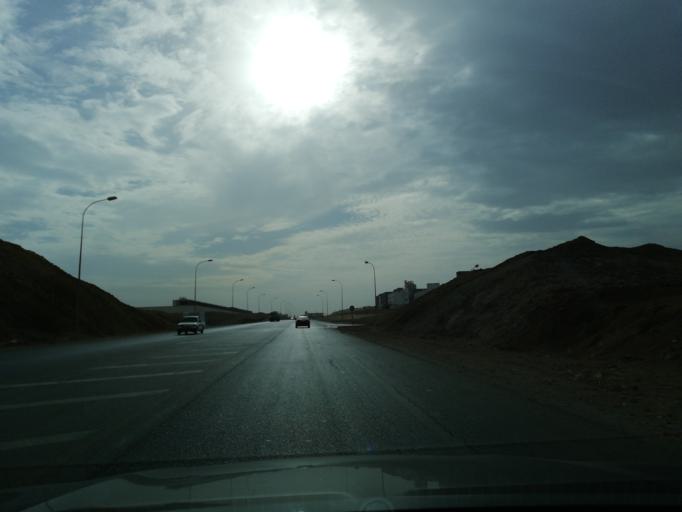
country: OM
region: Muhafazat Masqat
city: Bawshar
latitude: 23.4777
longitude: 58.2947
